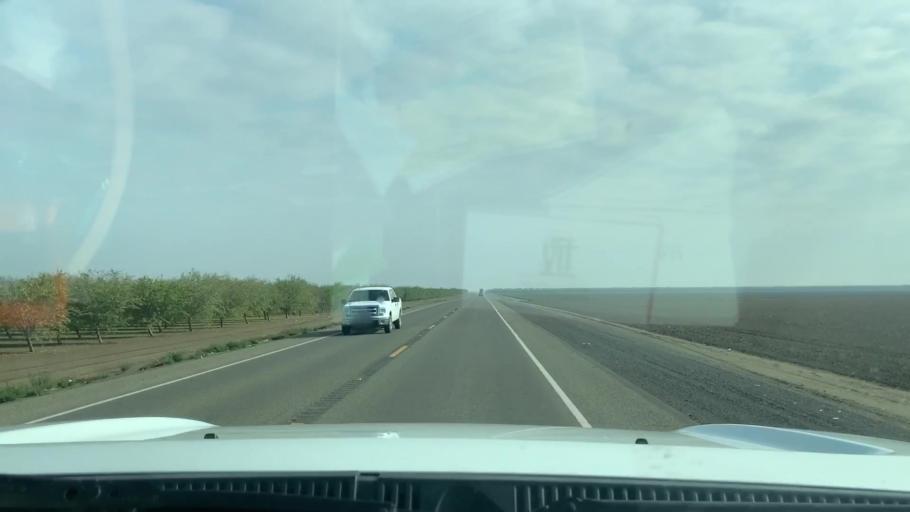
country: US
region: California
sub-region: Fresno County
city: Huron
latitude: 36.2554
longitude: -120.0594
